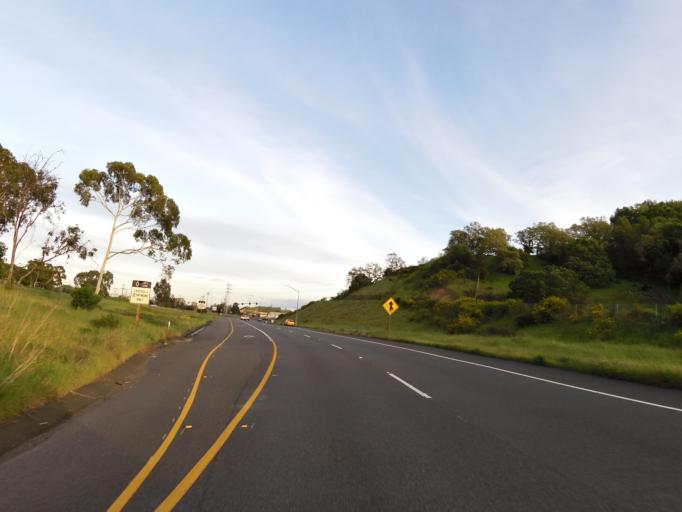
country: US
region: California
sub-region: Marin County
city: Novato
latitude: 38.0772
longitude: -122.5456
